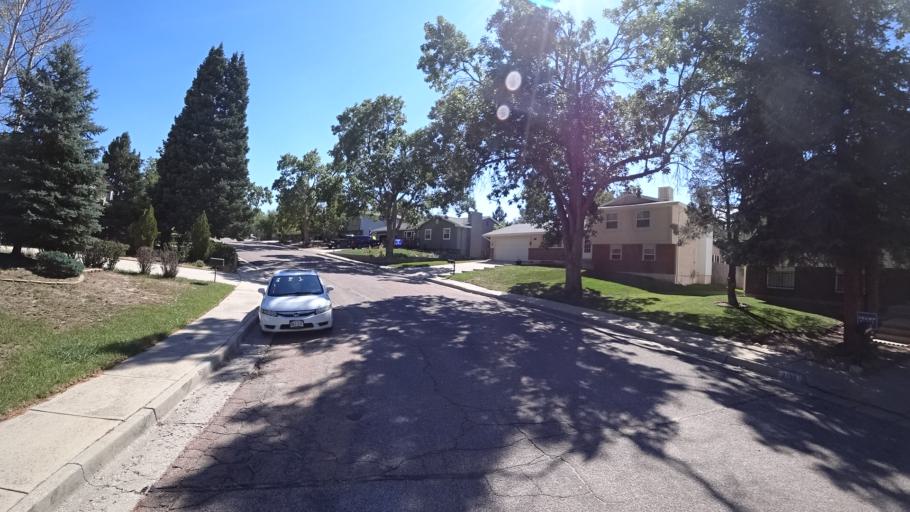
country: US
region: Colorado
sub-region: El Paso County
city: Cimarron Hills
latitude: 38.8772
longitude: -104.7330
